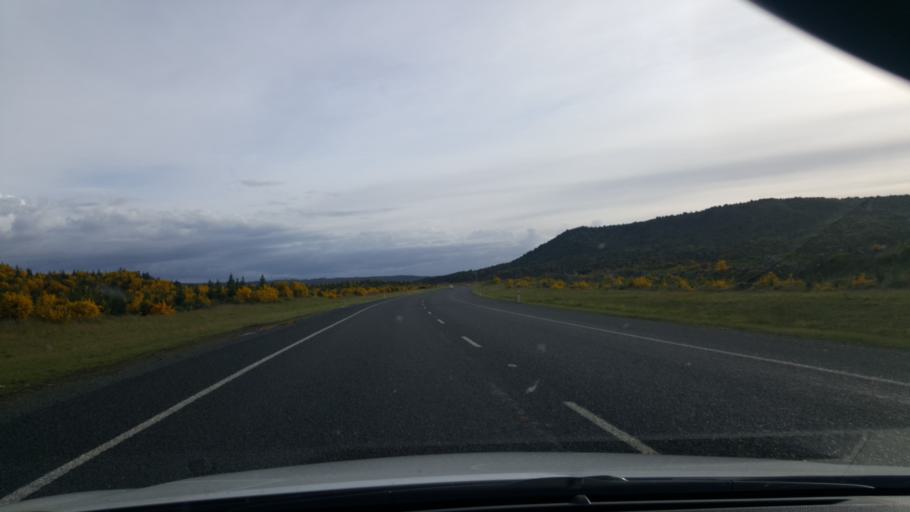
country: NZ
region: Waikato
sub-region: Taupo District
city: Taupo
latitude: -38.8396
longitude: 176.0634
